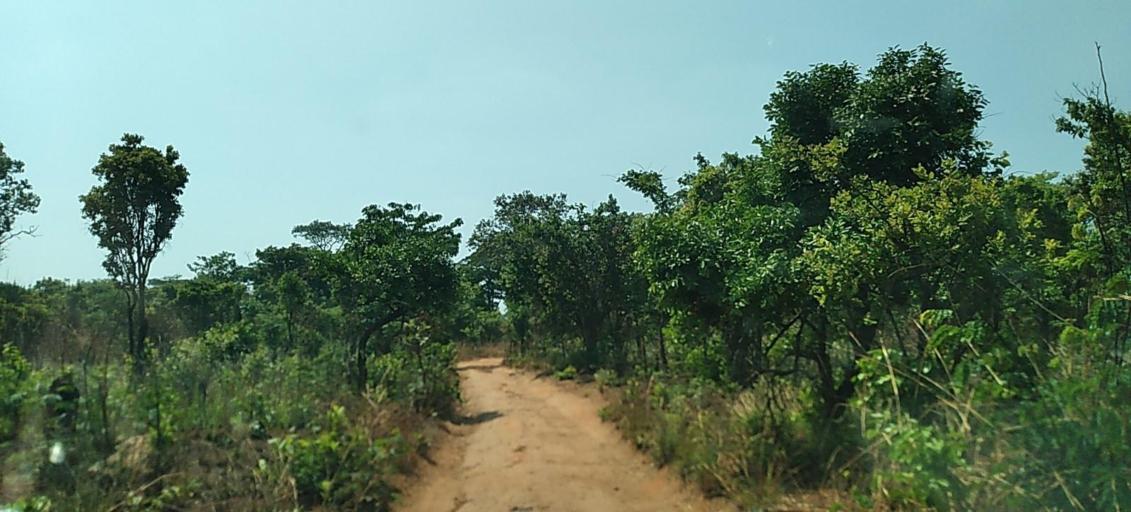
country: ZM
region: North-Western
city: Solwezi
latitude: -12.1026
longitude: 26.2889
